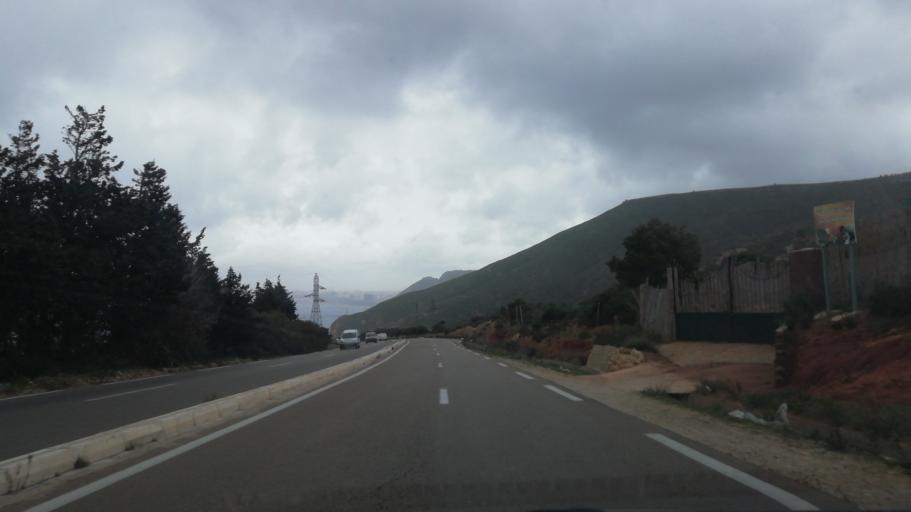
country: DZ
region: Oran
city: Mers el Kebir
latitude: 35.7196
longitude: -0.7371
